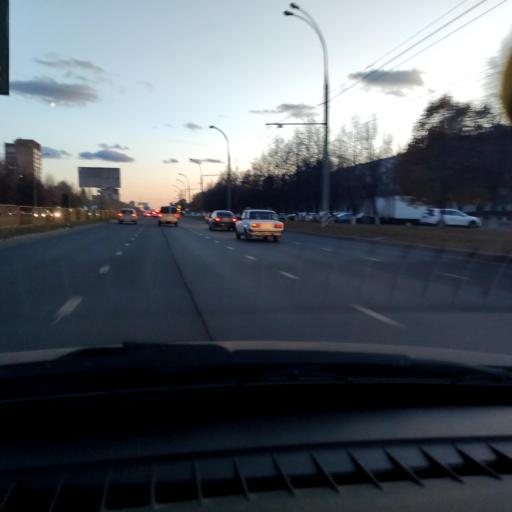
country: RU
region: Samara
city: Tol'yatti
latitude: 53.5241
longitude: 49.2960
